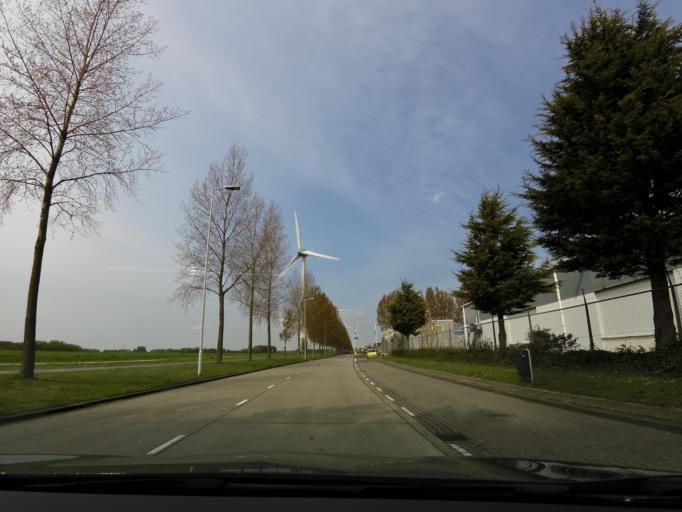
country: NL
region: South Holland
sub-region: Gemeente Maassluis
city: Maassluis
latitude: 51.8675
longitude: 4.2615
